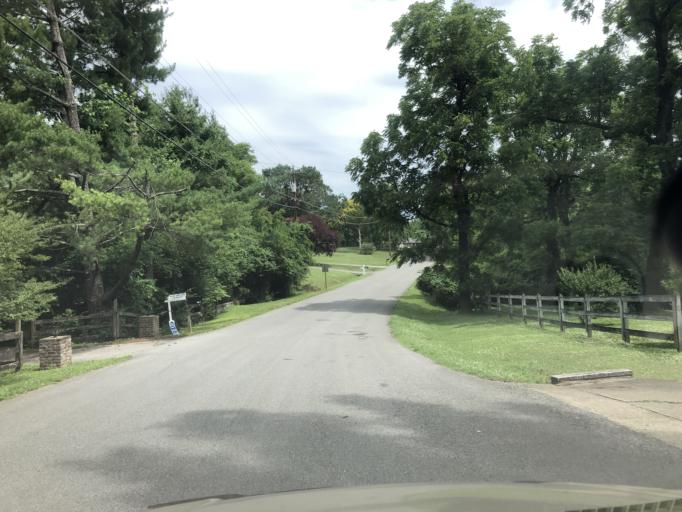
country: US
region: Tennessee
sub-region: Davidson County
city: Lakewood
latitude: 36.2567
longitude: -86.6097
